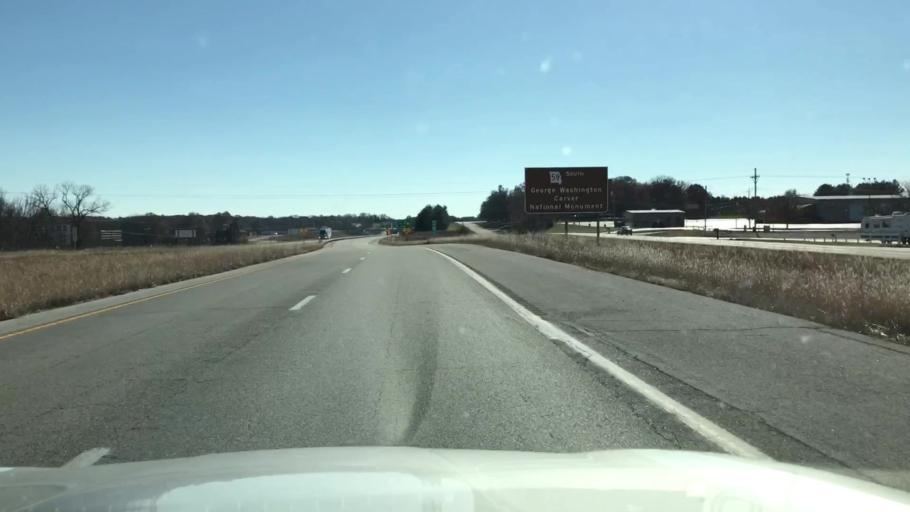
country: US
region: Missouri
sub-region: Jasper County
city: Carthage
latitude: 37.0907
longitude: -94.3125
